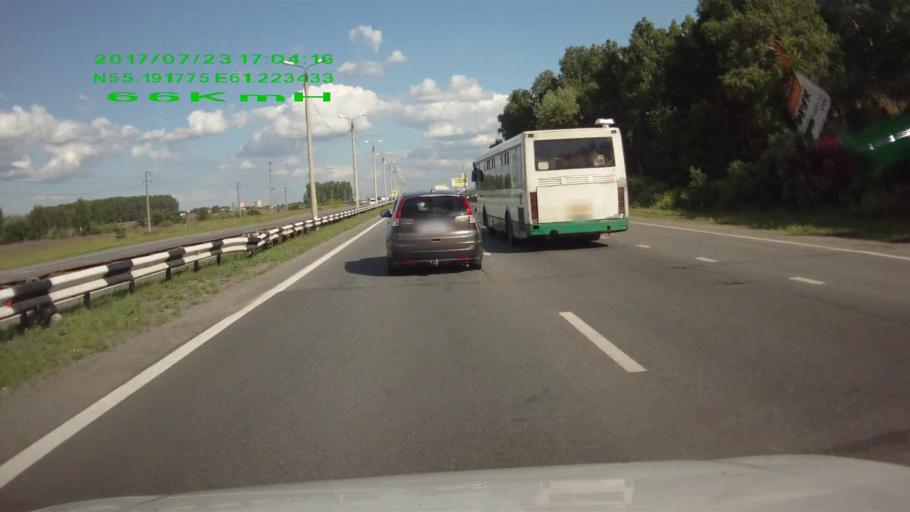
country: RU
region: Chelyabinsk
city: Roshchino
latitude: 55.1914
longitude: 61.2248
